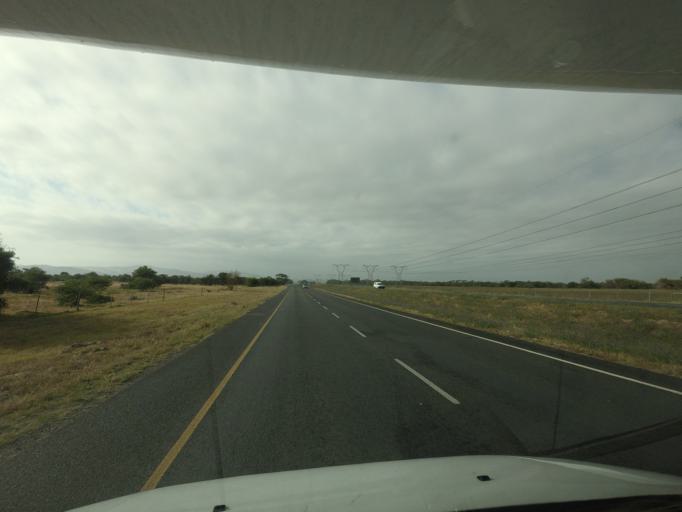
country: ZA
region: Western Cape
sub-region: City of Cape Town
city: Sunset Beach
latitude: -33.7377
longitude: 18.5455
